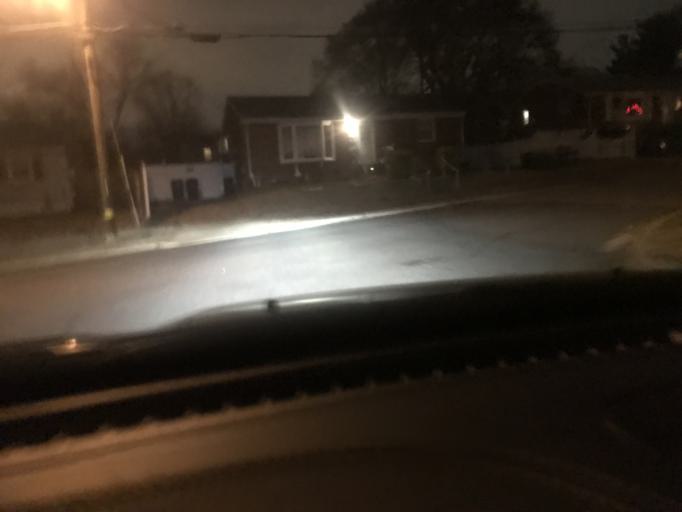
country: US
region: Maryland
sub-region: Prince George's County
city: Oxon Hill
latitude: 38.7990
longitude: -76.9867
